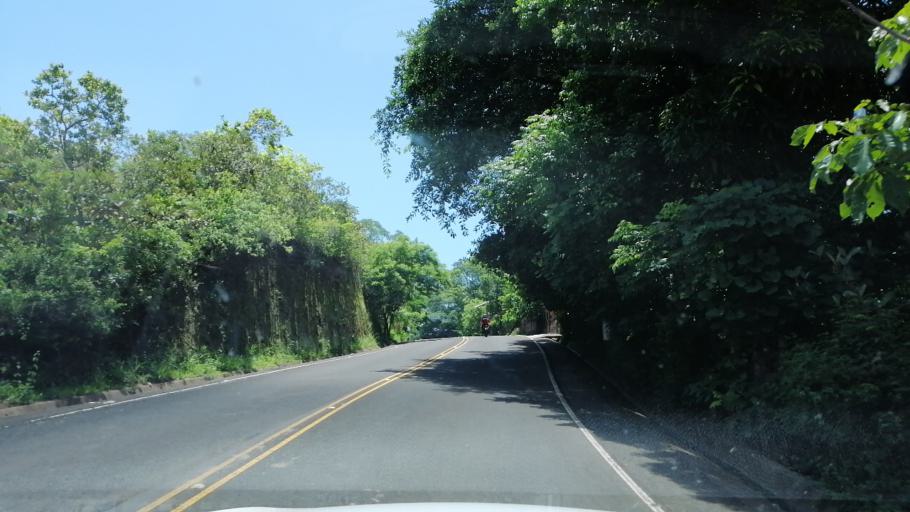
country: SV
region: San Miguel
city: Ciudad Barrios
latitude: 13.7927
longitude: -88.2868
